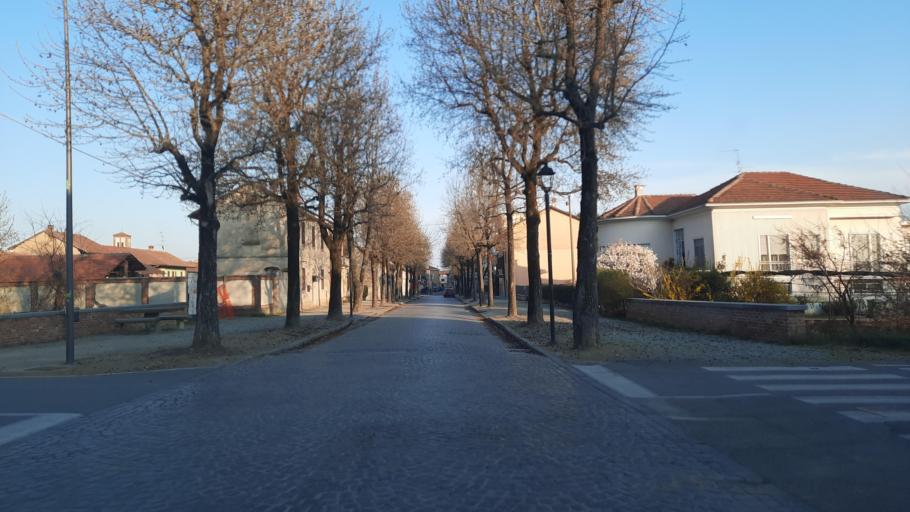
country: IT
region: Piedmont
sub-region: Provincia di Vercelli
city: Bianze
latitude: 45.3085
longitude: 8.1175
